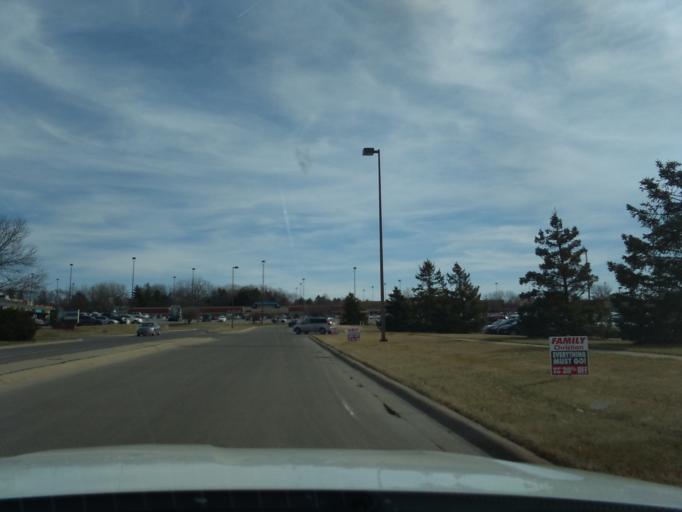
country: US
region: Nebraska
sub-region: Lancaster County
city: Lincoln
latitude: 40.7586
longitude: -96.6440
